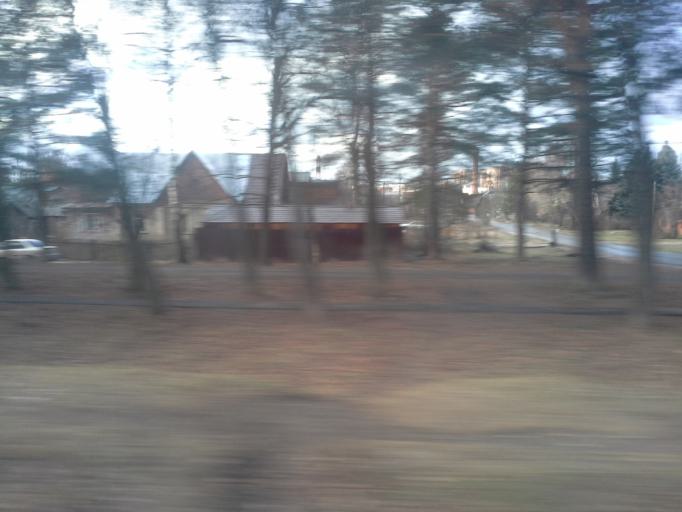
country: RU
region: Moskovskaya
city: Cherkizovo
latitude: 55.9389
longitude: 37.7899
